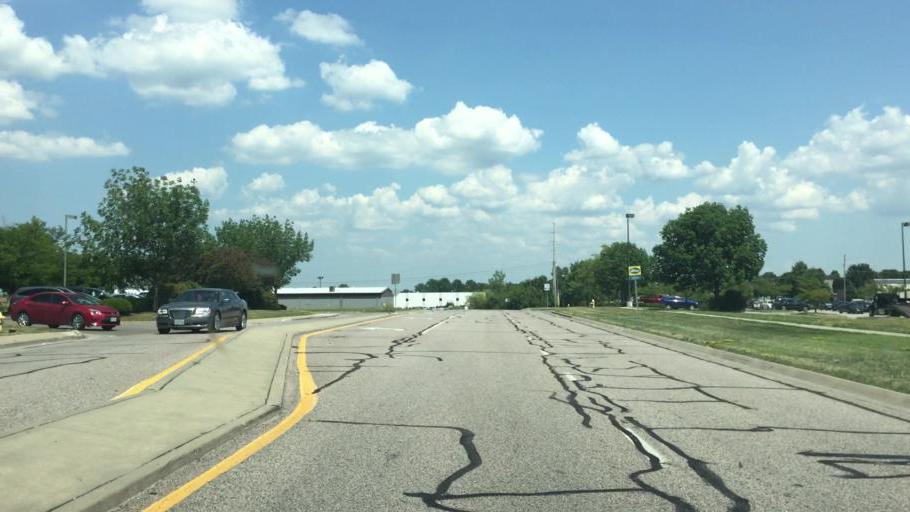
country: US
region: Missouri
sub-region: Jackson County
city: Lees Summit
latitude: 38.9009
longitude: -94.3625
